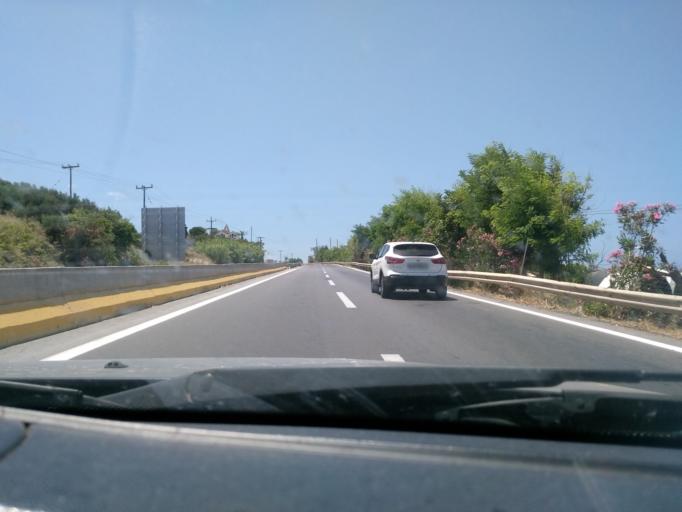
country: GR
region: Crete
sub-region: Nomos Rethymnis
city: Rethymno
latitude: 35.3640
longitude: 24.5076
